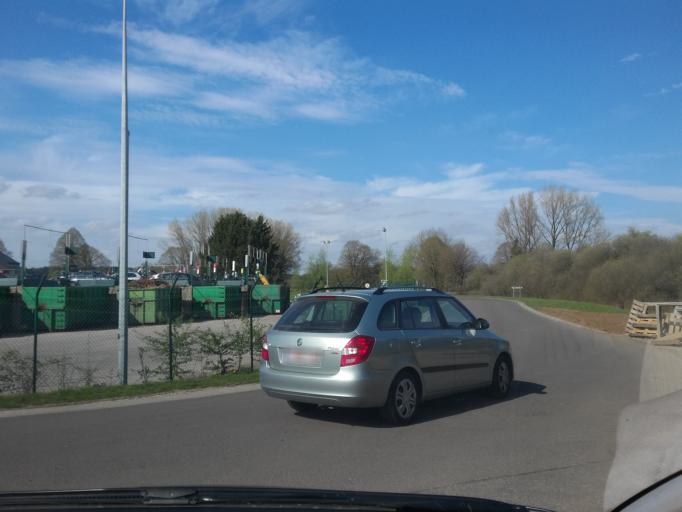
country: BE
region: Wallonia
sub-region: Province du Luxembourg
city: Arlon
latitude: 49.6907
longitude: 5.7769
